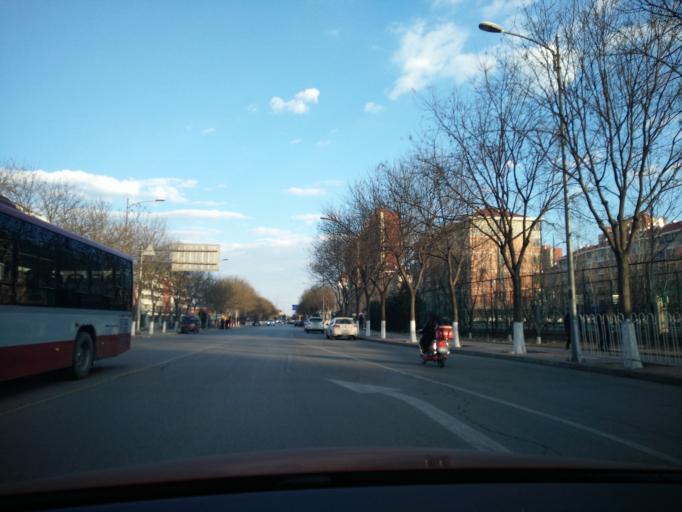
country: CN
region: Beijing
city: Yinghai
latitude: 39.7599
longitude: 116.4929
